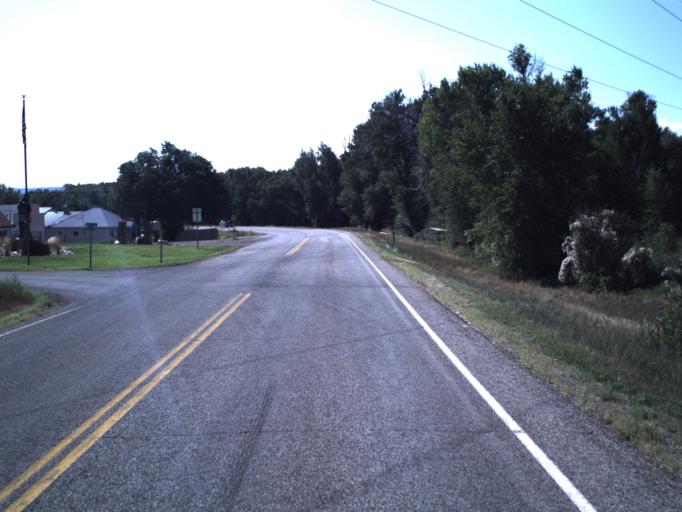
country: US
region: Utah
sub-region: Duchesne County
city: Duchesne
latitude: 40.3547
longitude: -110.7142
